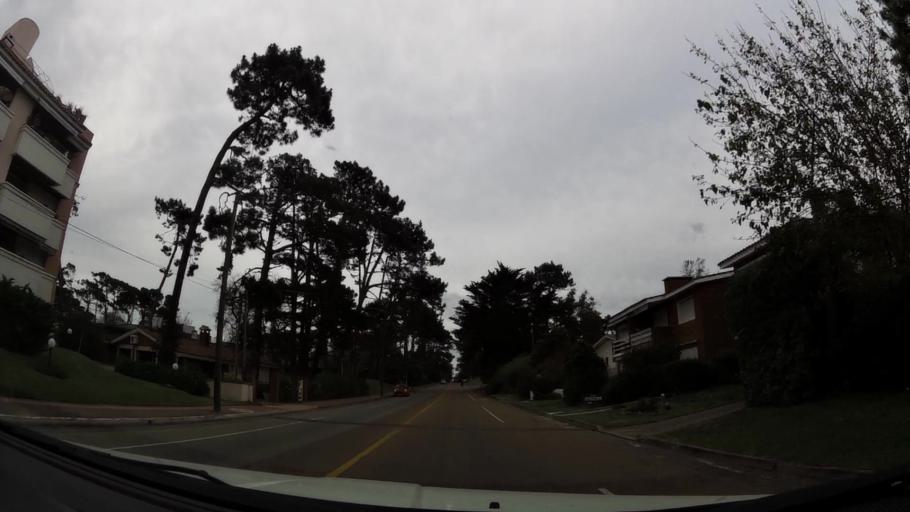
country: UY
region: Maldonado
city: Maldonado
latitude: -34.9289
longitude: -54.9561
